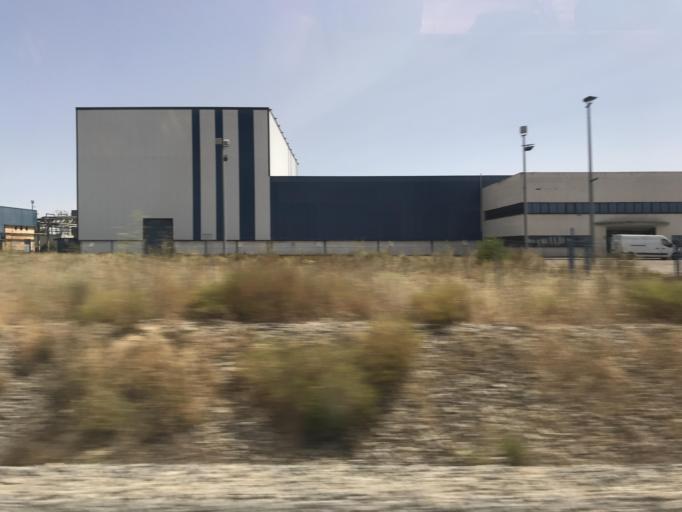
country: ES
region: Castille and Leon
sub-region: Provincia de Palencia
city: Duenas
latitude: 41.8559
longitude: -4.5503
